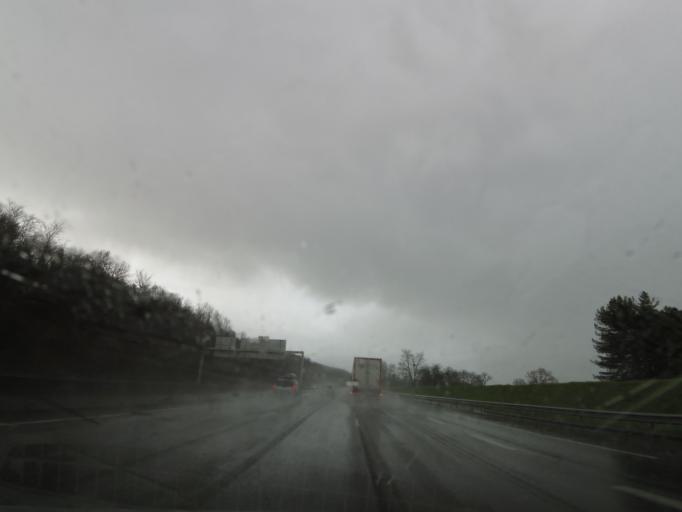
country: FR
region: Bourgogne
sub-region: Departement de Saone-et-Loire
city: Sance
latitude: 46.3563
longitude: 4.8289
